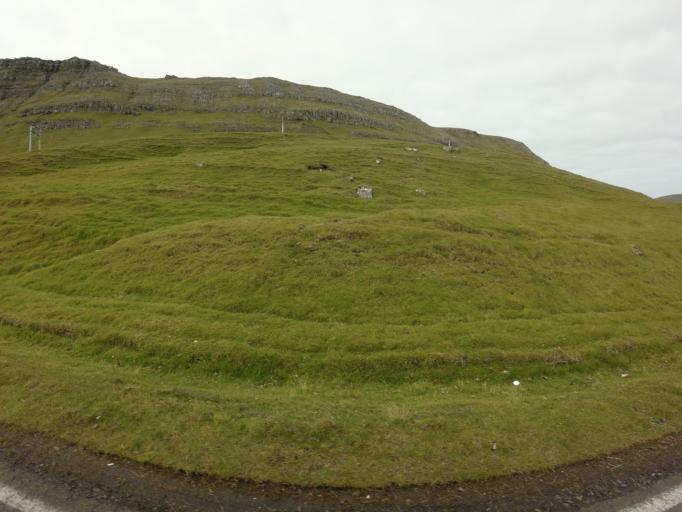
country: FO
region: Suduroy
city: Tvoroyri
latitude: 61.5900
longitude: -6.9468
